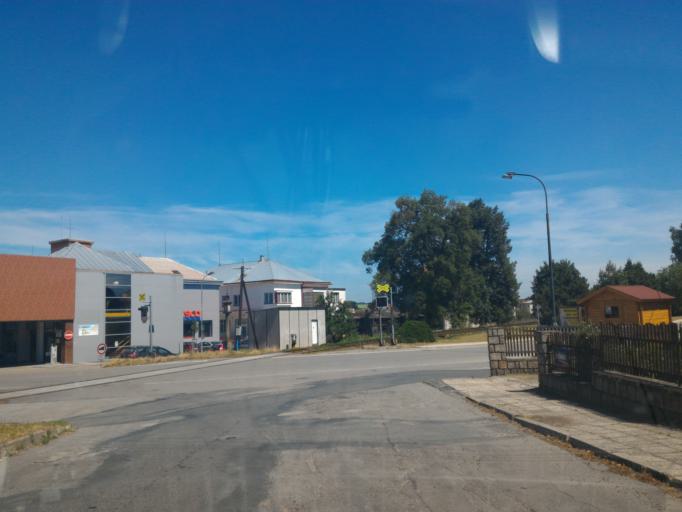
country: CZ
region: Vysocina
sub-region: Okres Jihlava
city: Telc
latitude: 49.1851
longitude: 15.4660
